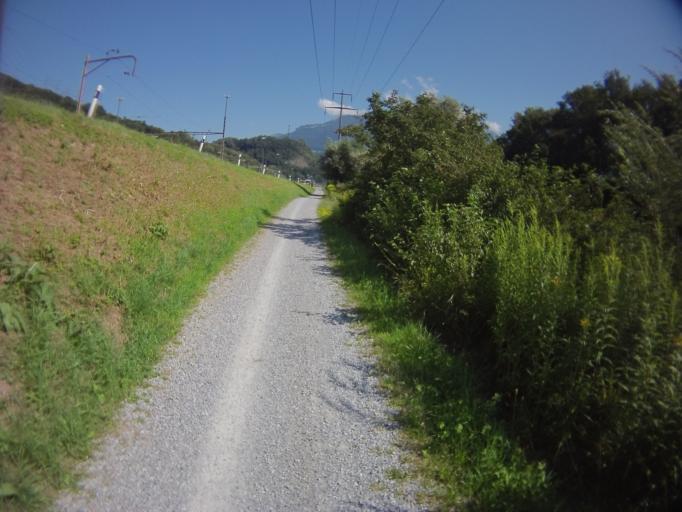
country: CH
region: Glarus
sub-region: Glarus
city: Niederurnen
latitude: 47.1386
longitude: 9.0552
